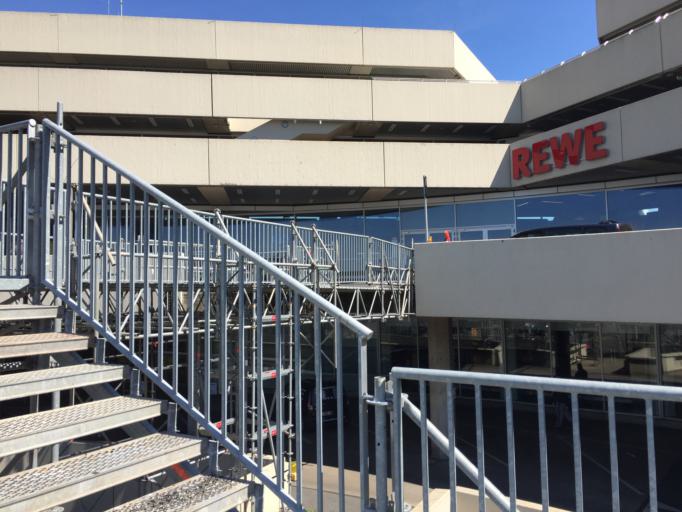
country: DE
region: North Rhine-Westphalia
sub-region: Regierungsbezirk Koln
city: Wahn-Heide
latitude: 50.8787
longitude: 7.1221
